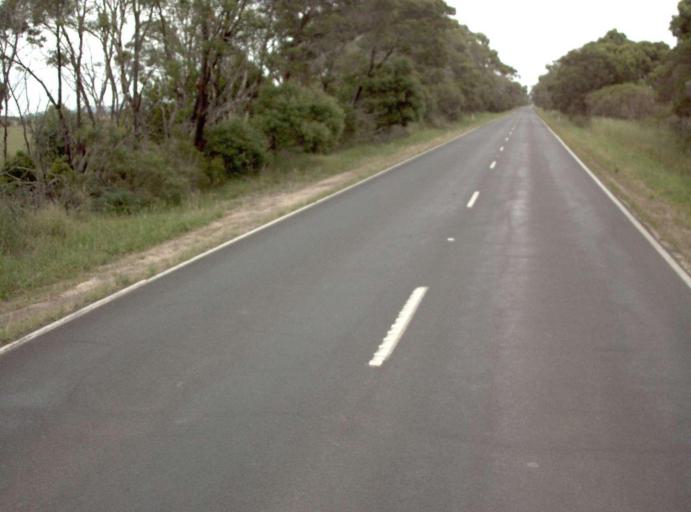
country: AU
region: Victoria
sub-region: Latrobe
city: Traralgon
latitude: -38.5529
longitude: 146.7490
